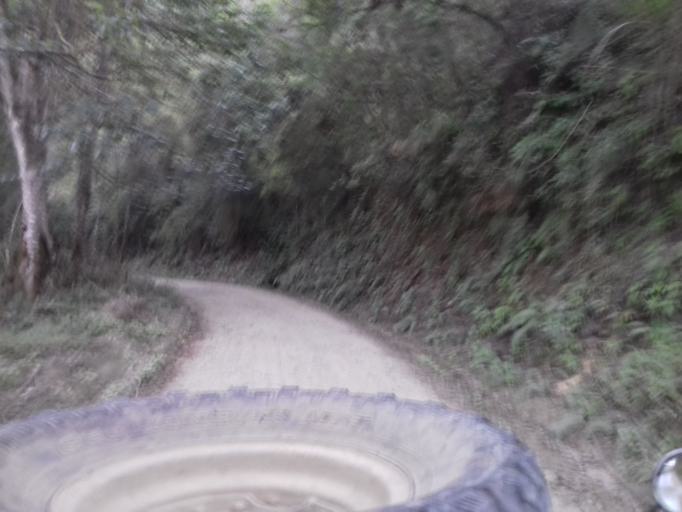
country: CO
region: Quindio
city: Salento
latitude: 4.6148
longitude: -75.5512
